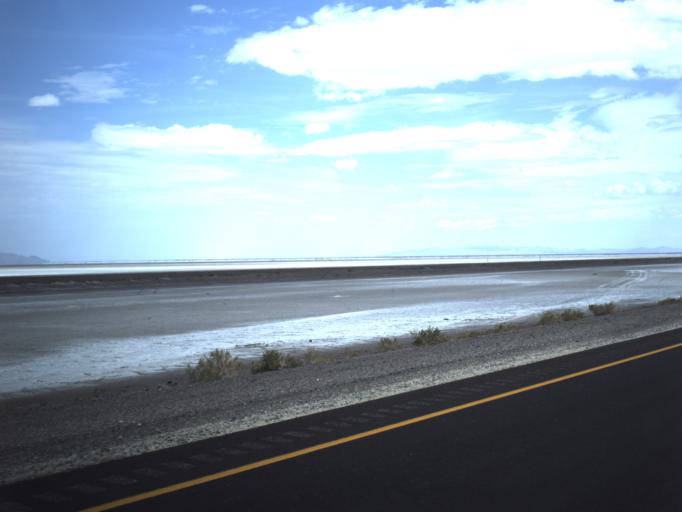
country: US
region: Utah
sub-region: Tooele County
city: Wendover
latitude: 40.7335
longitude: -113.6144
